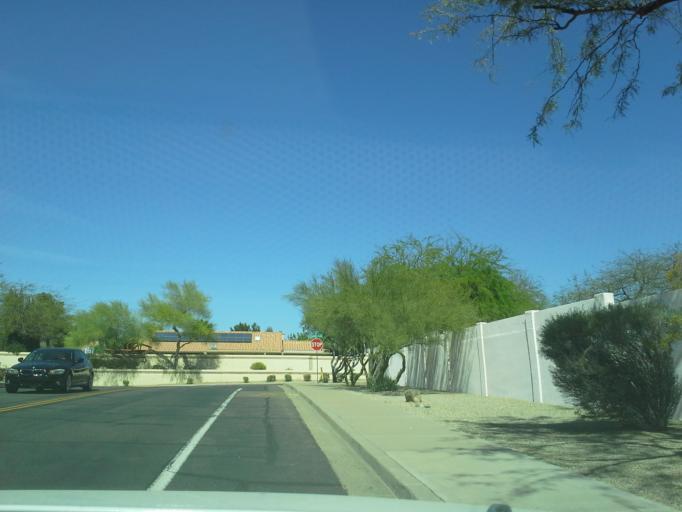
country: US
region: Arizona
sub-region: Maricopa County
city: Scottsdale
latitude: 33.6037
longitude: -111.8566
